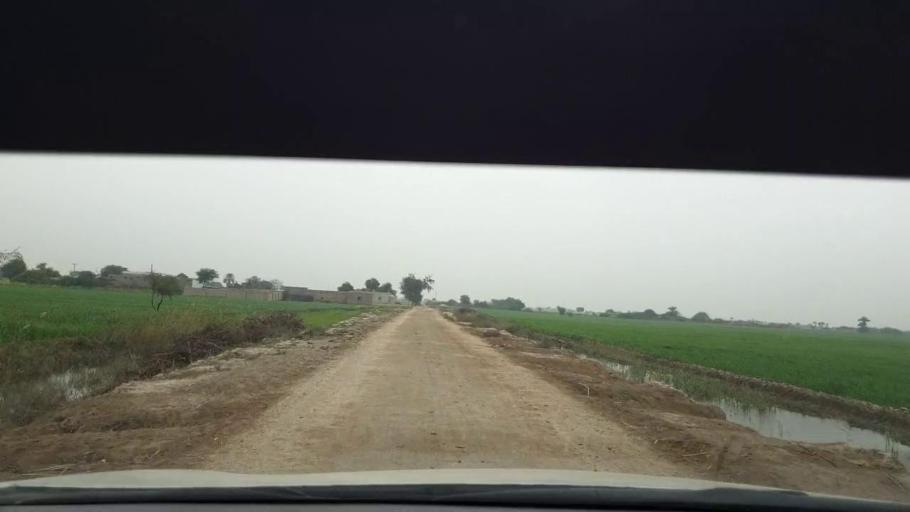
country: PK
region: Sindh
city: Berani
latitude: 25.7580
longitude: 68.8528
